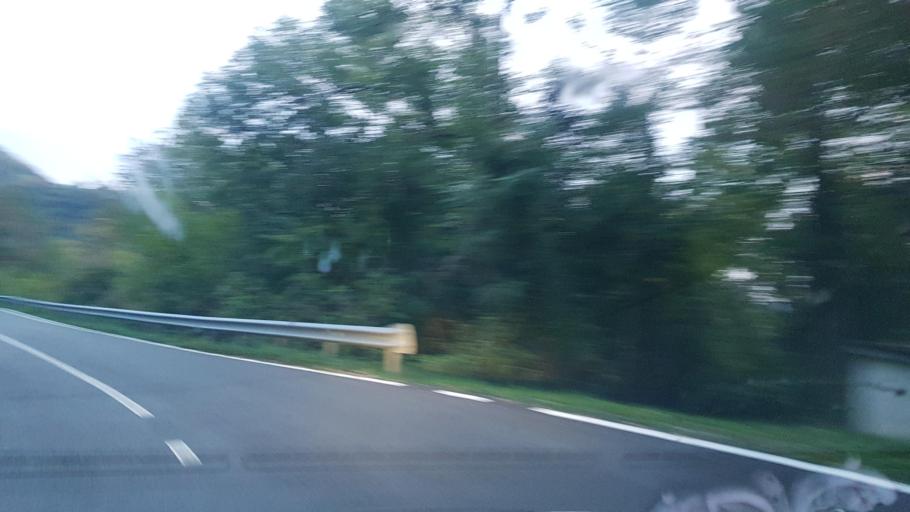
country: IT
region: Friuli Venezia Giulia
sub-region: Provincia di Pordenone
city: Anduins
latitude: 46.2305
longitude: 12.9579
